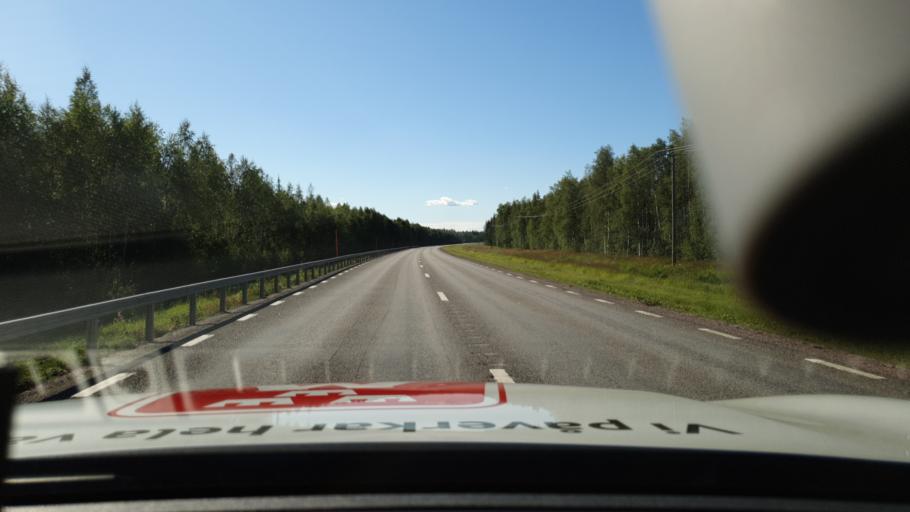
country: SE
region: Norrbotten
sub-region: Pitea Kommun
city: Rosvik
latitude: 65.5784
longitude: 21.7059
